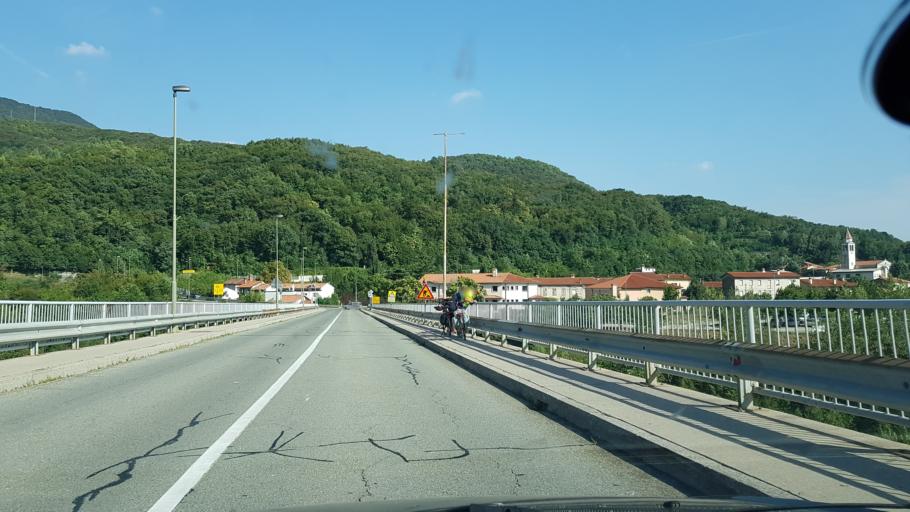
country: SI
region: Nova Gorica
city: Solkan
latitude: 45.9762
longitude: 13.6473
